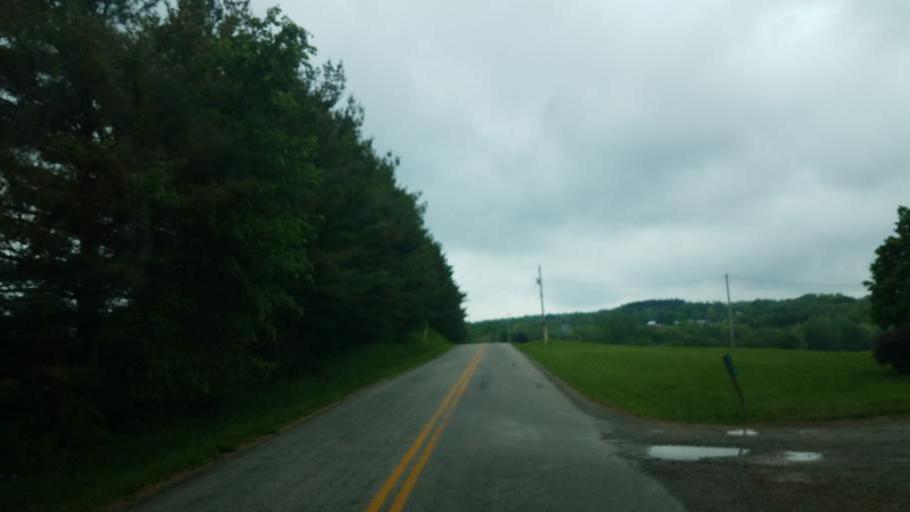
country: US
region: Ohio
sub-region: Ashland County
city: Ashland
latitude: 40.7593
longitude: -82.3394
